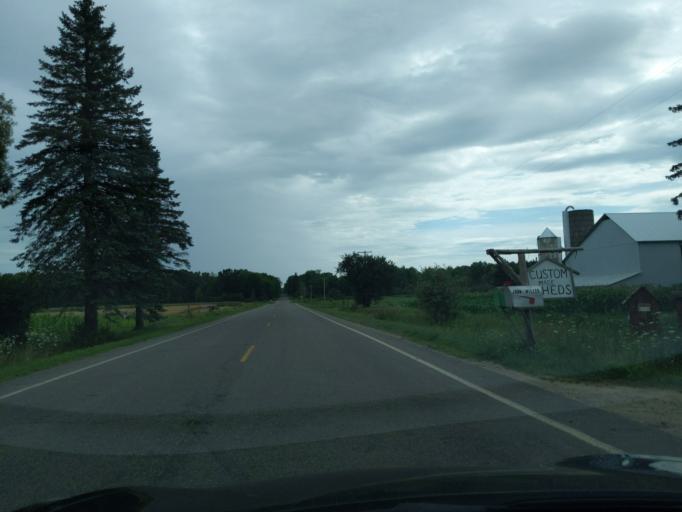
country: US
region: Michigan
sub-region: Clare County
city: Harrison
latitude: 44.0057
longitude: -84.9491
